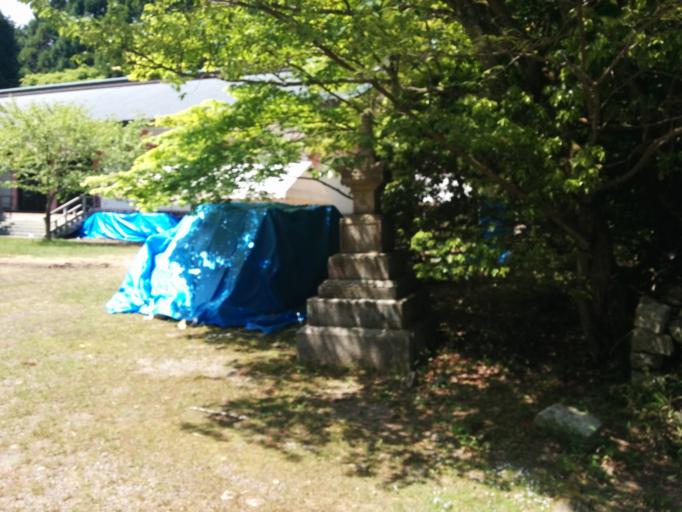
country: JP
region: Shiga Prefecture
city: Otsu-shi
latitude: 35.0955
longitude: 135.8513
